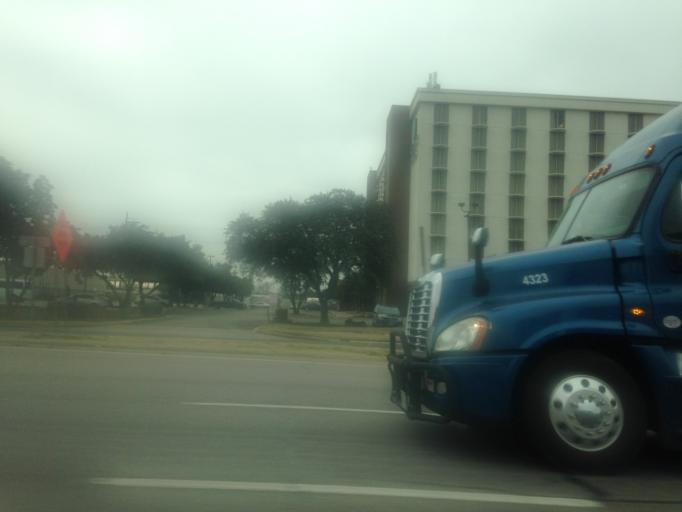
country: US
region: Texas
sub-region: Dallas County
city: Dallas
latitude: 32.8085
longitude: -96.8445
